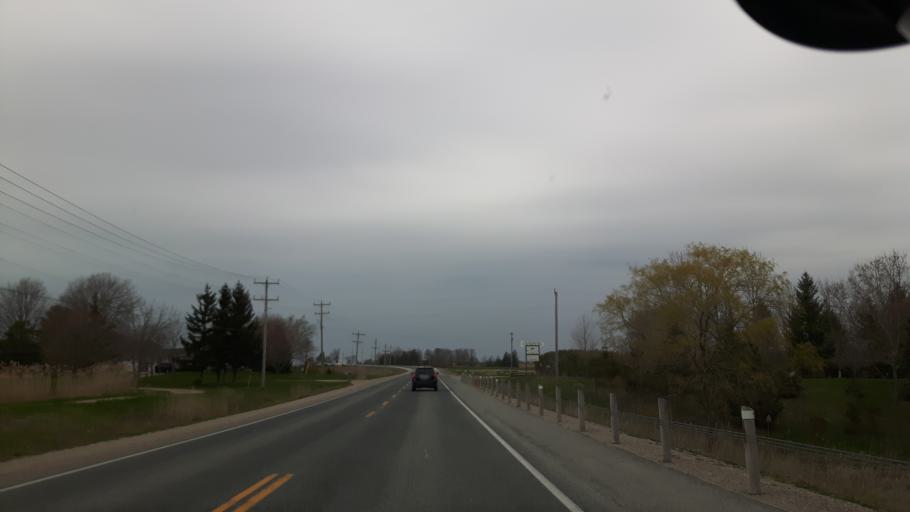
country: CA
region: Ontario
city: Goderich
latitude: 43.6866
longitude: -81.6313
